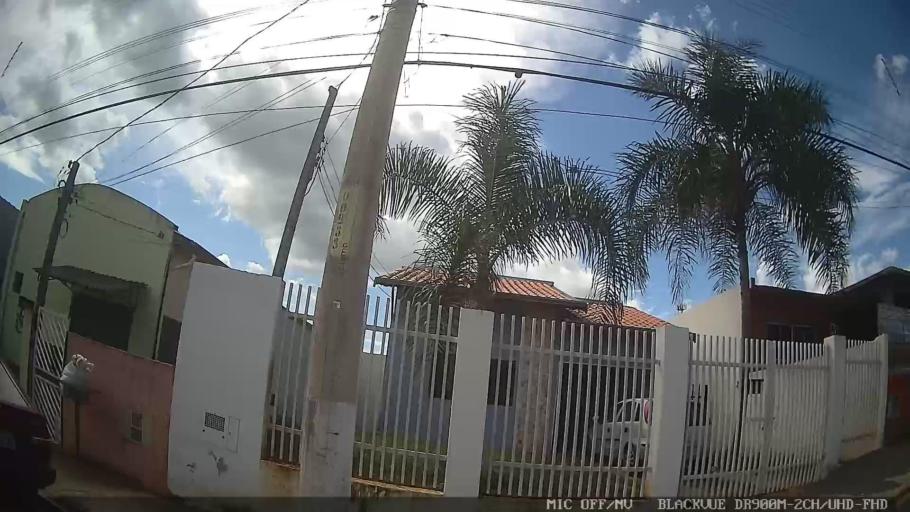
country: BR
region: Sao Paulo
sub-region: Conchas
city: Conchas
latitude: -23.0195
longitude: -48.0141
